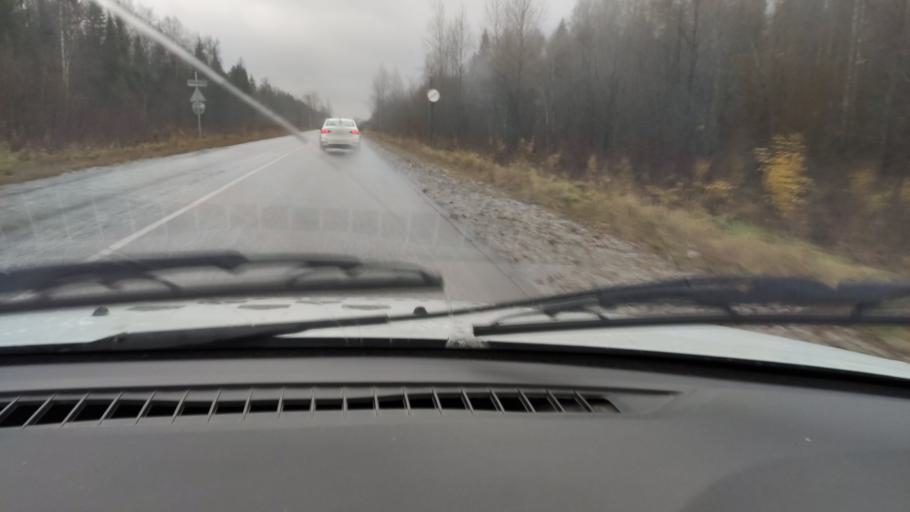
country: RU
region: Perm
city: Novyye Lyady
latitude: 58.0350
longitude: 56.6051
